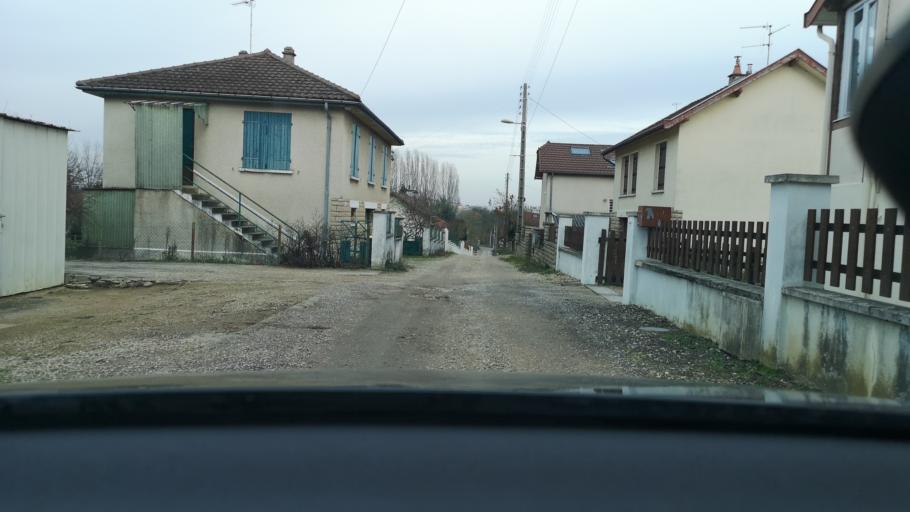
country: FR
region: Bourgogne
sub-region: Departement de Saone-et-Loire
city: Saint-Remy
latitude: 46.7753
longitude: 4.8269
